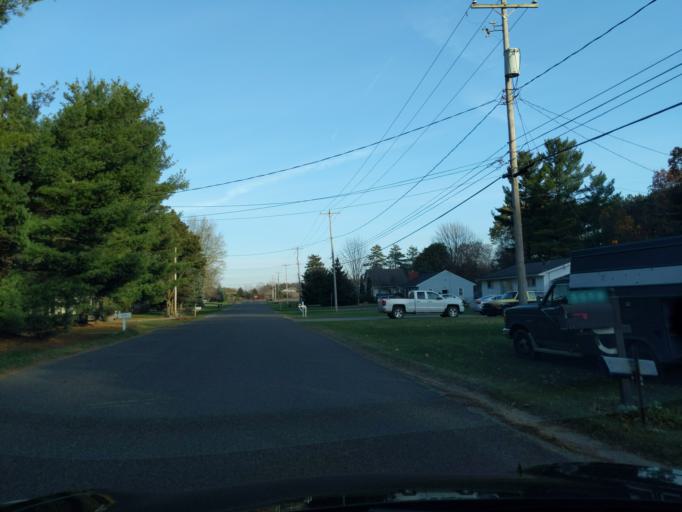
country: US
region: Michigan
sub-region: Clinton County
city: Bath
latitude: 42.7955
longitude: -84.4521
